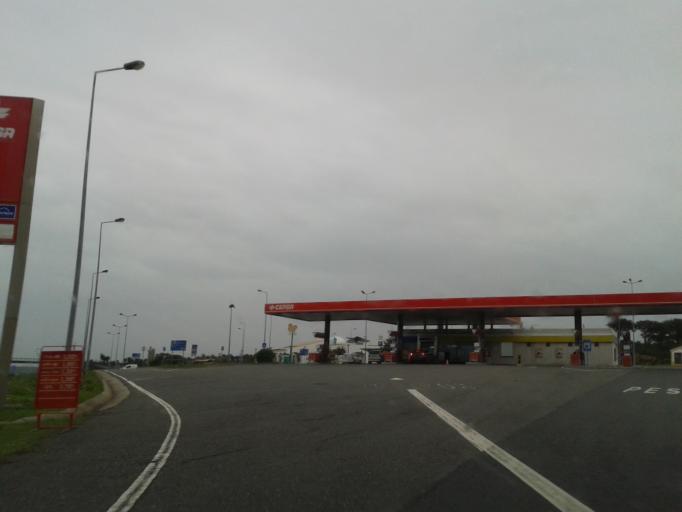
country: PT
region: Beja
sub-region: Almodovar
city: Almodovar
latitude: 37.5352
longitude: -8.1830
